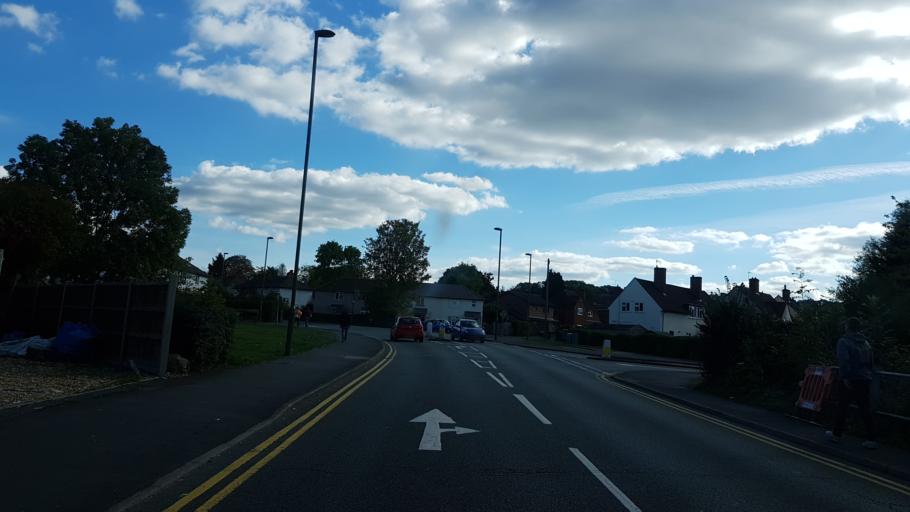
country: GB
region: England
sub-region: Surrey
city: Guildford
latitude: 51.2403
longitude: -0.5952
